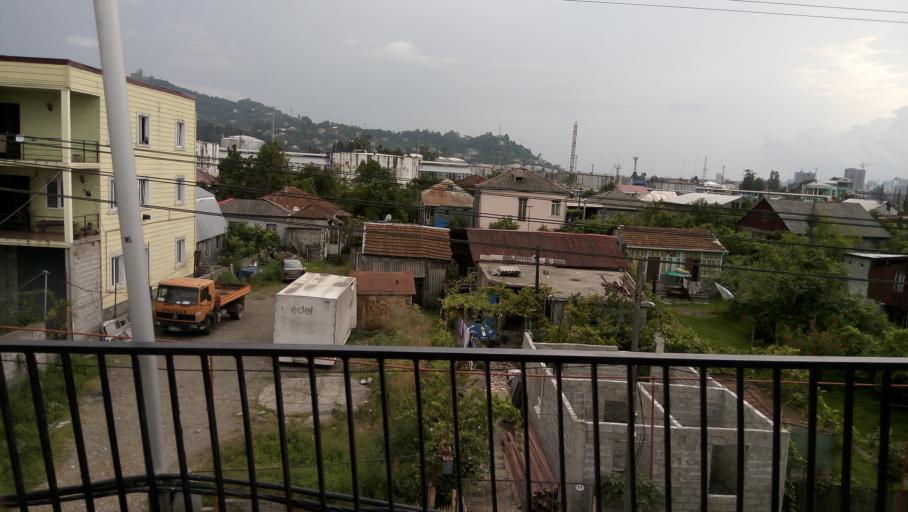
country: GE
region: Ajaria
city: Batumi
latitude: 41.6473
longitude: 41.6677
